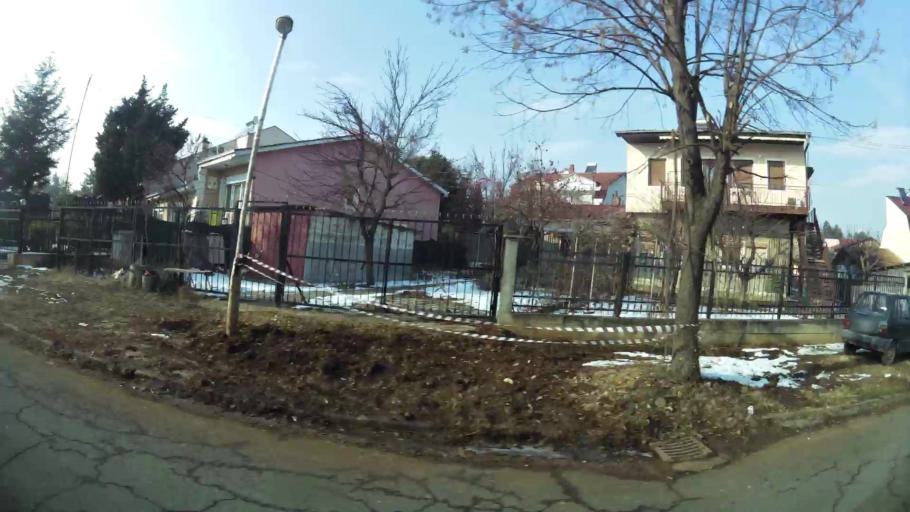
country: MK
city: Creshevo
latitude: 42.0057
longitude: 21.4972
